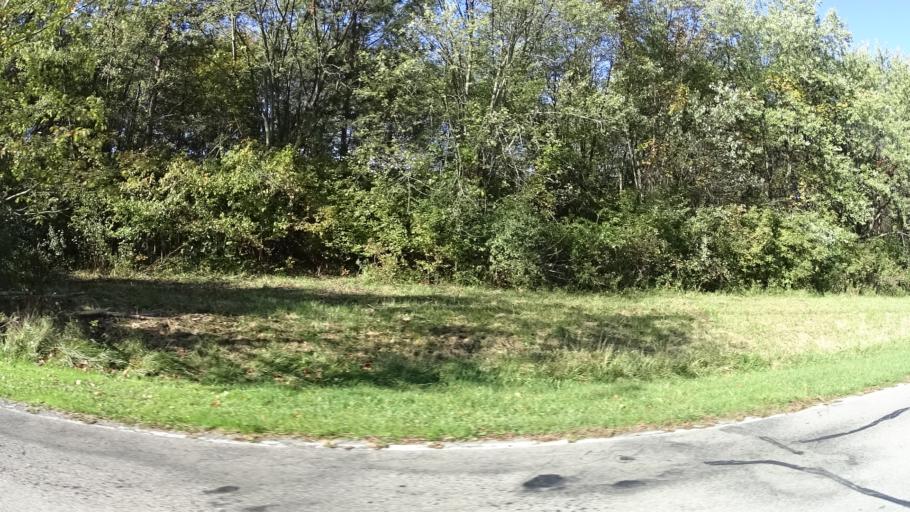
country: US
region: Ohio
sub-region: Lorain County
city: Vermilion-on-the-Lake
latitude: 41.3983
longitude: -82.3262
